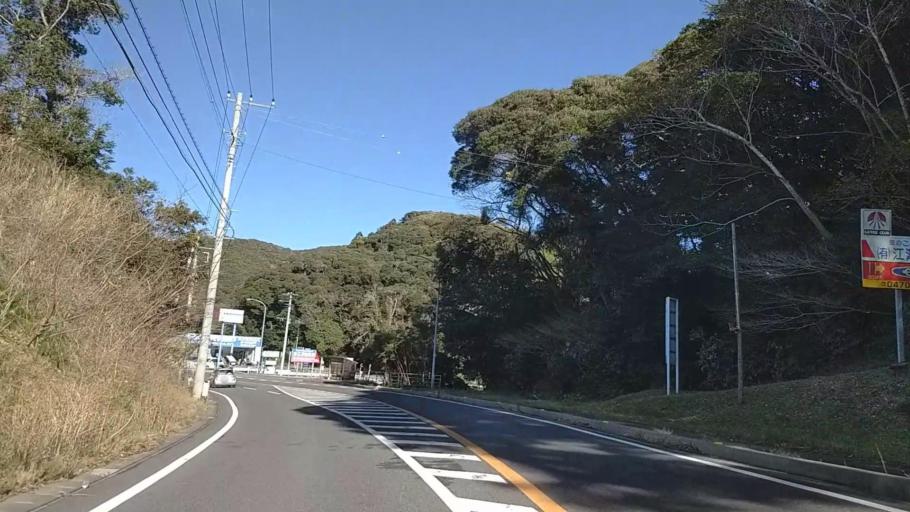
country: JP
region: Chiba
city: Katsuura
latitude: 35.1585
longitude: 140.3269
